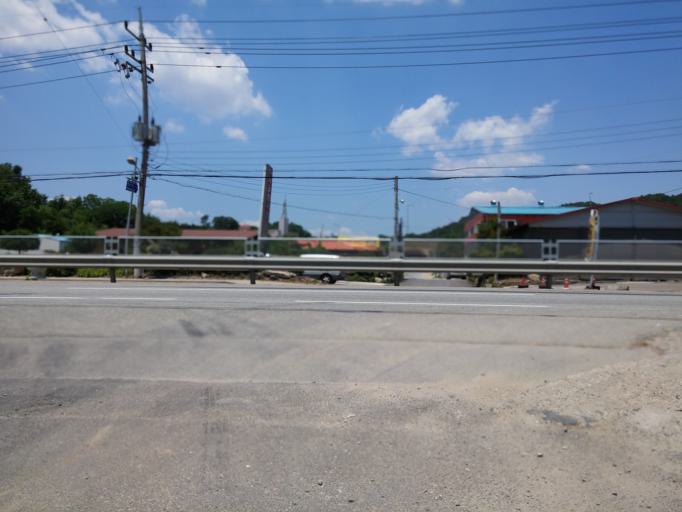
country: KR
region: Chungcheongbuk-do
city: Cheongju-si
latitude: 36.5621
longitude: 127.4386
